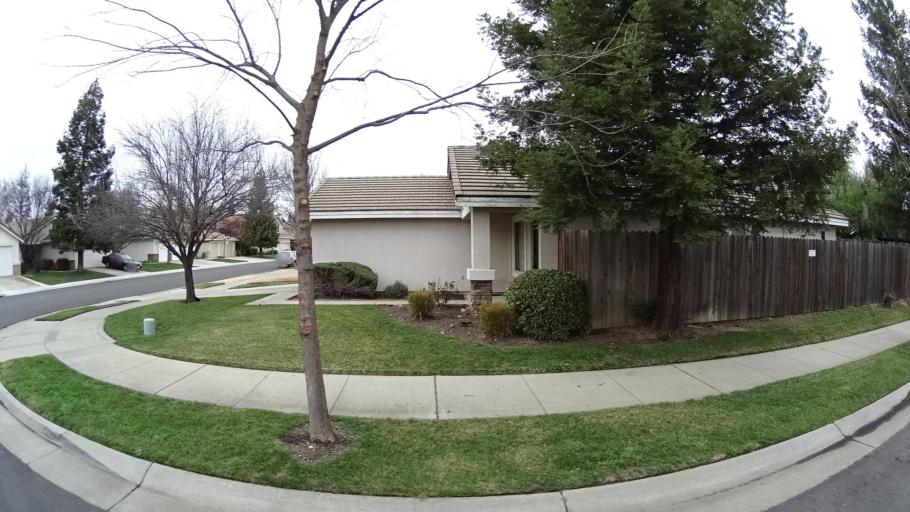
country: US
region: California
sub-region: Yolo County
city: Davis
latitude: 38.5551
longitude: -121.7028
